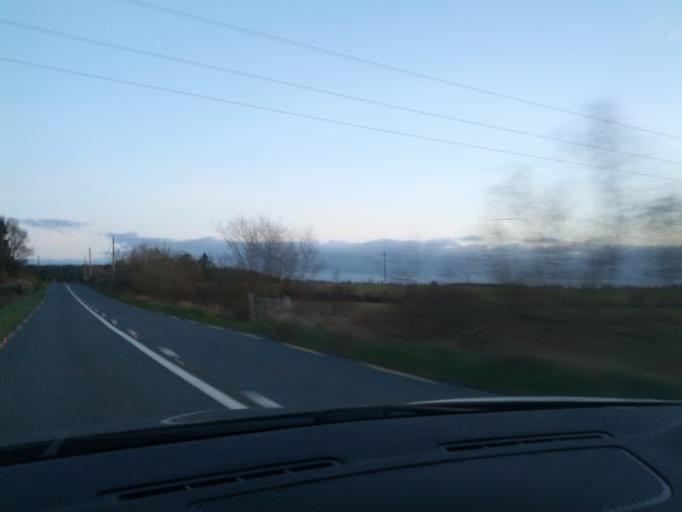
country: IE
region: Connaught
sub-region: Roscommon
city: Boyle
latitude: 53.9154
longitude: -8.2718
